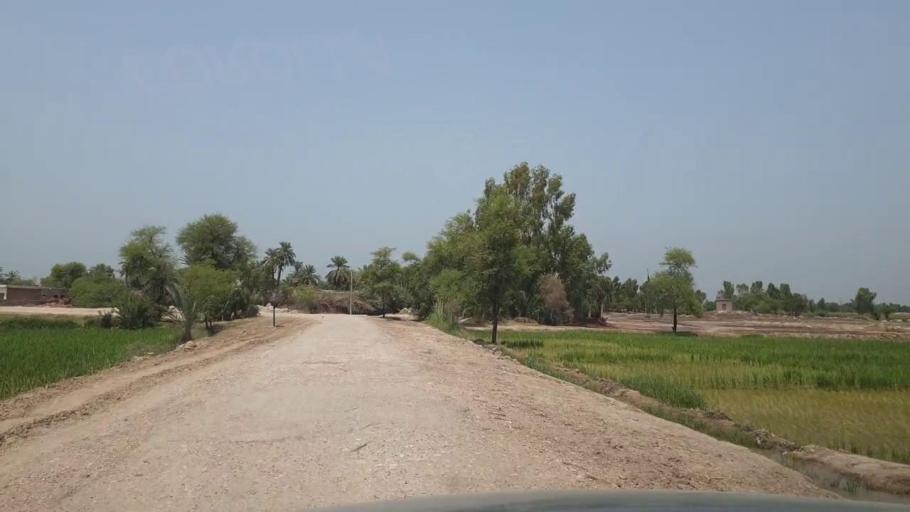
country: PK
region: Sindh
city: Garhi Yasin
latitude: 27.8693
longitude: 68.4556
